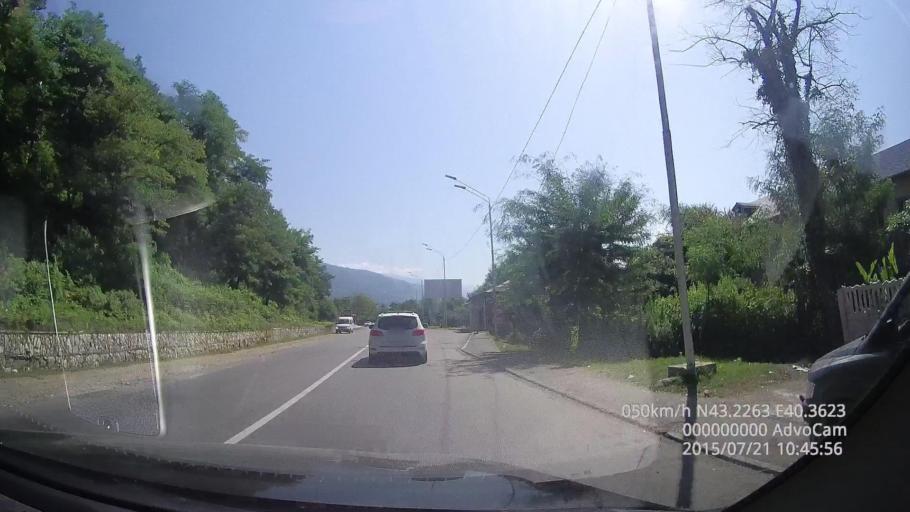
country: GE
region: Abkhazia
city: Bich'vinta
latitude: 43.2265
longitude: 40.3628
